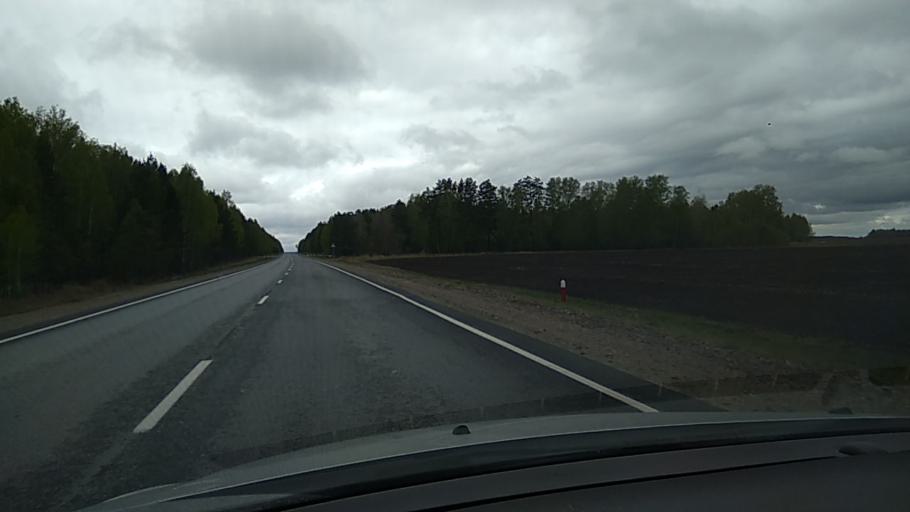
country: RU
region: Kurgan
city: Shadrinsk
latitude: 56.1075
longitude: 64.0876
